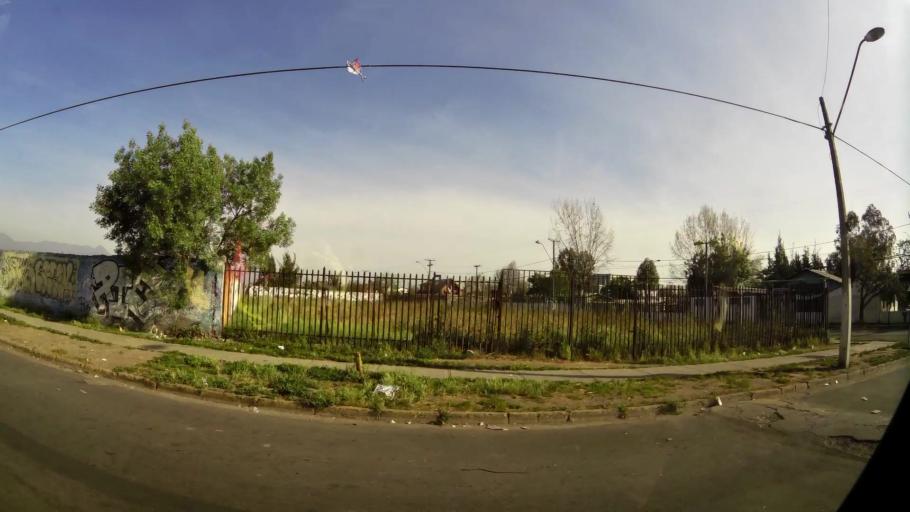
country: CL
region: Santiago Metropolitan
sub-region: Provincia de Santiago
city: Santiago
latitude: -33.5094
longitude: -70.6231
